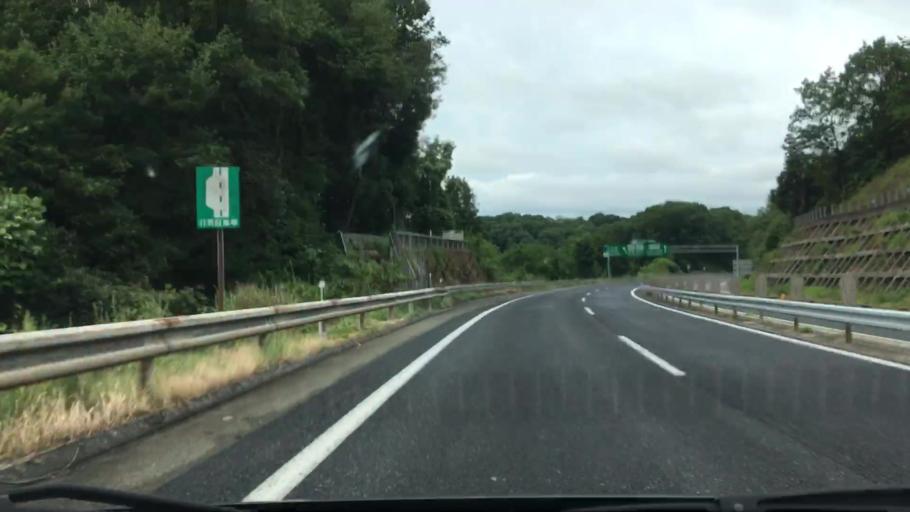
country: JP
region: Hiroshima
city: Miyoshi
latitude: 34.8049
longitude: 132.9185
